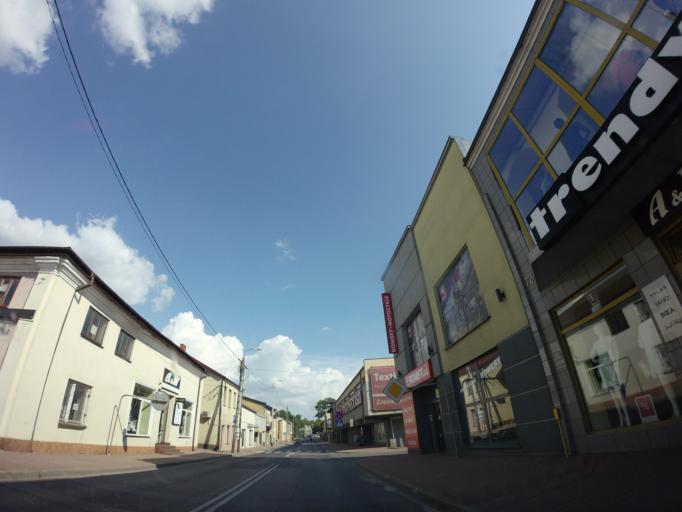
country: PL
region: Masovian Voivodeship
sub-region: Powiat sokolowski
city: Sokolow Podlaski
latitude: 52.4050
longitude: 22.2549
